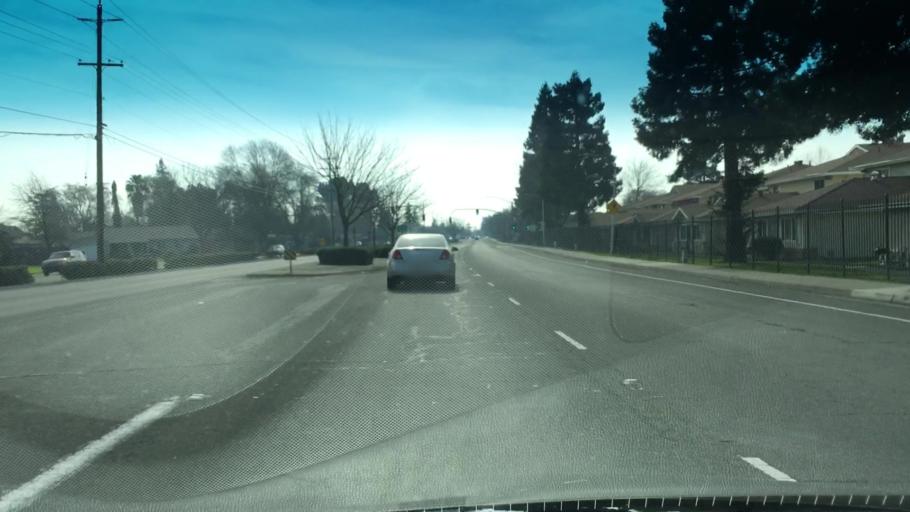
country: US
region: California
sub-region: Sacramento County
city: Parkway
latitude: 38.4890
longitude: -121.4556
